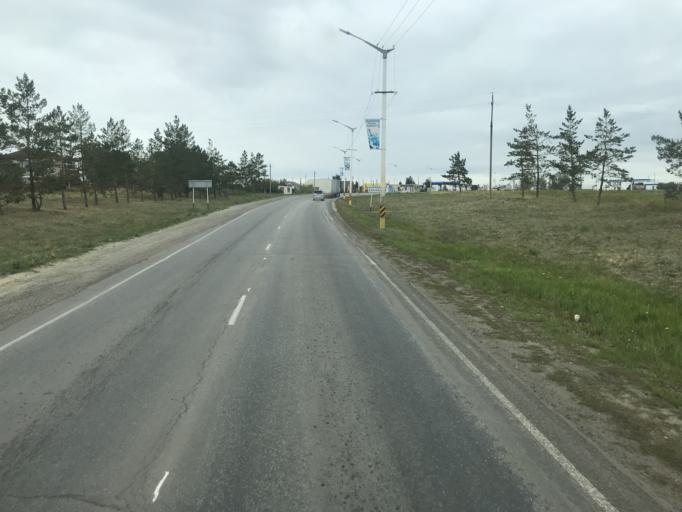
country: KZ
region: Qostanay
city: Komsomolets
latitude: 53.7610
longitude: 62.0765
